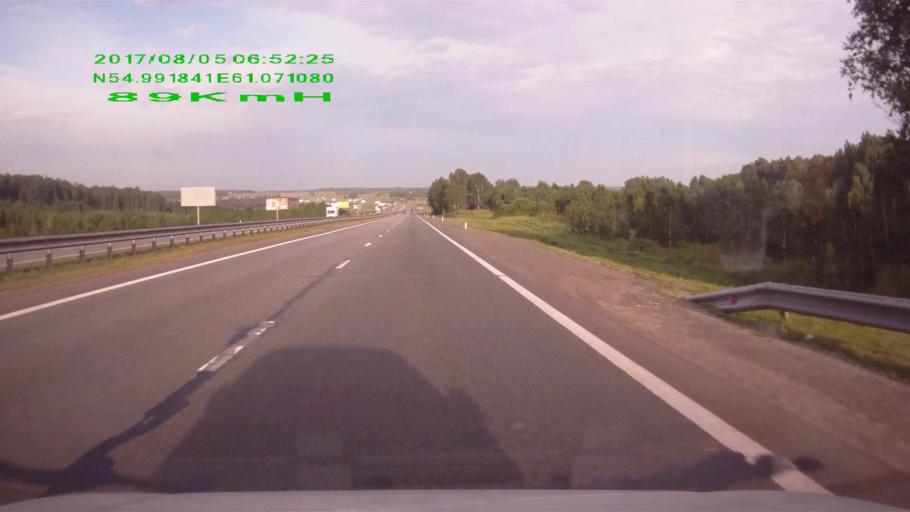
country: RU
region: Chelyabinsk
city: Poletayevo
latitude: 54.9918
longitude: 61.0701
